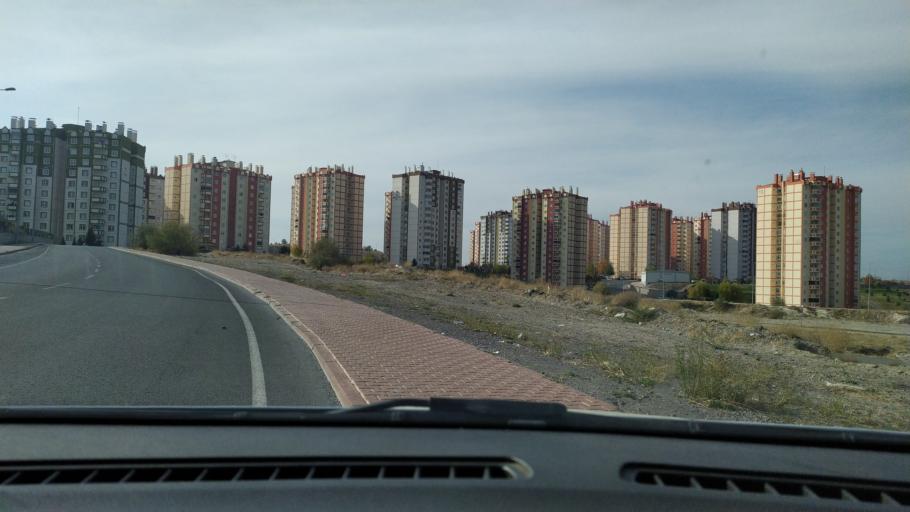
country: TR
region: Kayseri
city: Melikgazi
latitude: 38.7342
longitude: 35.3834
